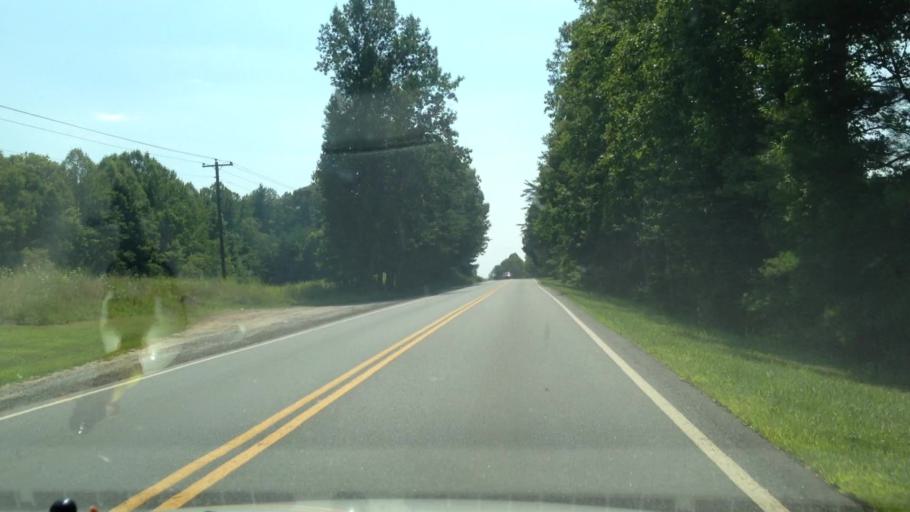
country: US
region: Virginia
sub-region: Patrick County
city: Stuart
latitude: 36.5868
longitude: -80.3957
